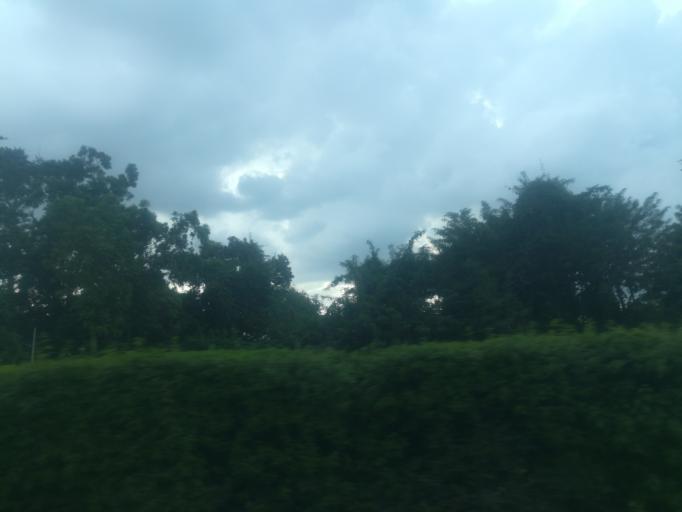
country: NG
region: Oyo
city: Ibadan
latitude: 7.4424
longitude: 3.9049
